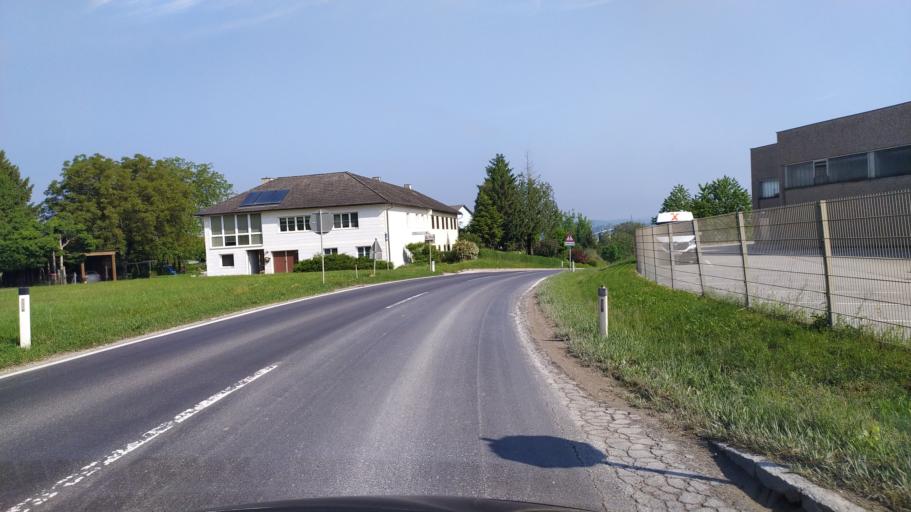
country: AT
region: Lower Austria
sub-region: Politischer Bezirk Amstetten
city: Ennsdorf
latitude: 48.2164
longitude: 14.5398
